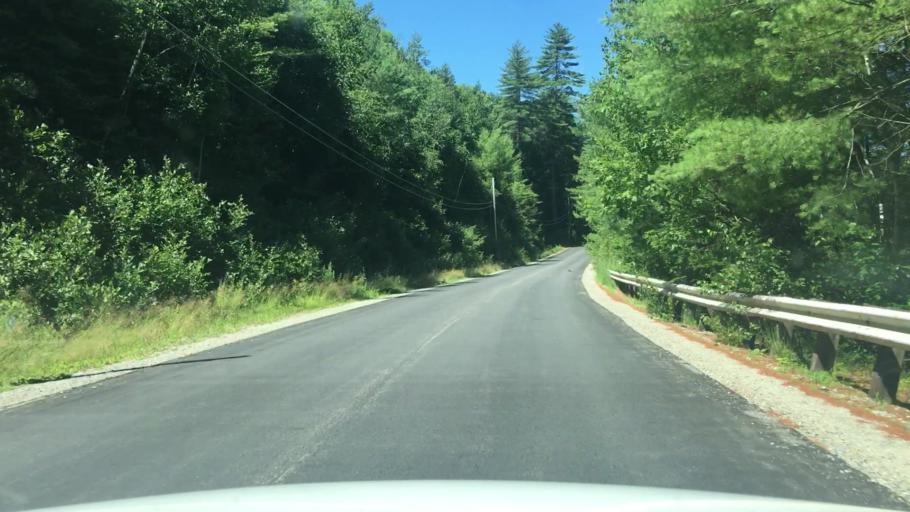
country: US
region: New Hampshire
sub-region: Merrimack County
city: Hopkinton
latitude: 43.2384
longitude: -71.6301
